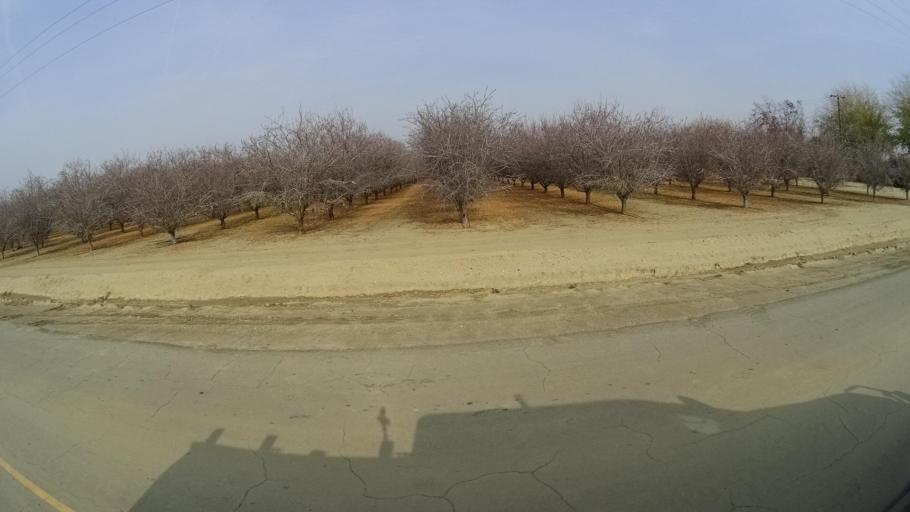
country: US
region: California
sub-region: Kern County
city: Greenfield
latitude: 35.0779
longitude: -119.0397
